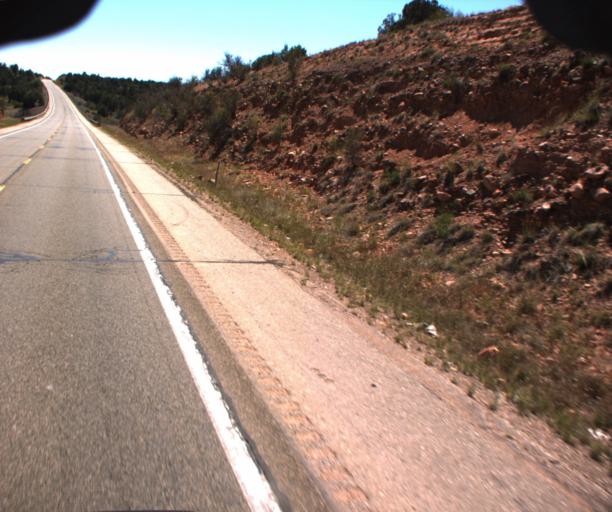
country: US
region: Arizona
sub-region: Yavapai County
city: Paulden
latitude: 34.9812
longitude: -112.4009
